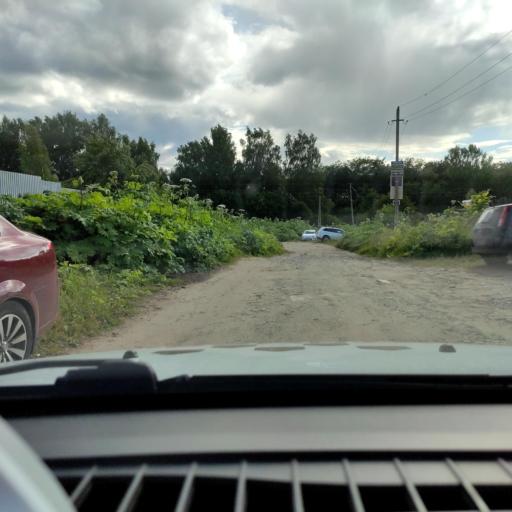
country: RU
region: Perm
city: Overyata
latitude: 58.0994
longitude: 55.8575
